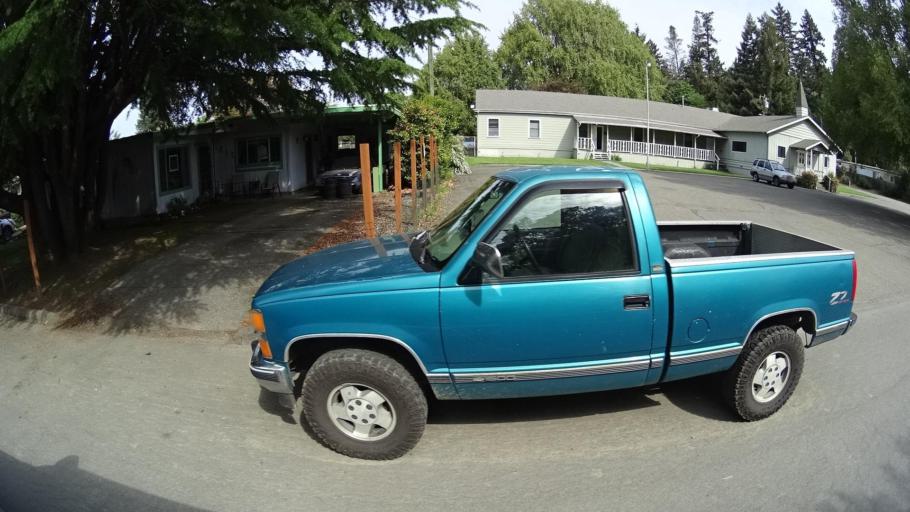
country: US
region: California
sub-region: Humboldt County
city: Redway
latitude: 40.1166
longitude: -123.8215
